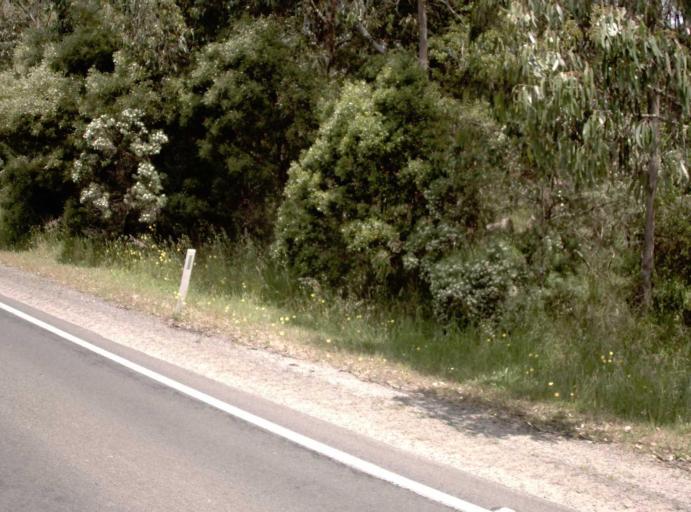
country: AU
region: Victoria
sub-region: Latrobe
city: Traralgon
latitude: -38.3487
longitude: 146.7148
